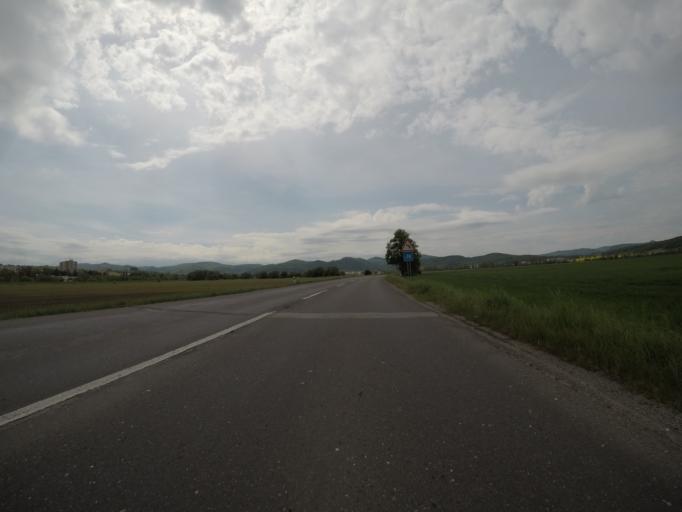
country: SK
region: Banskobystricky
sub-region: Okres Banska Bystrica
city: Zvolen
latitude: 48.5993
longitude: 19.1246
